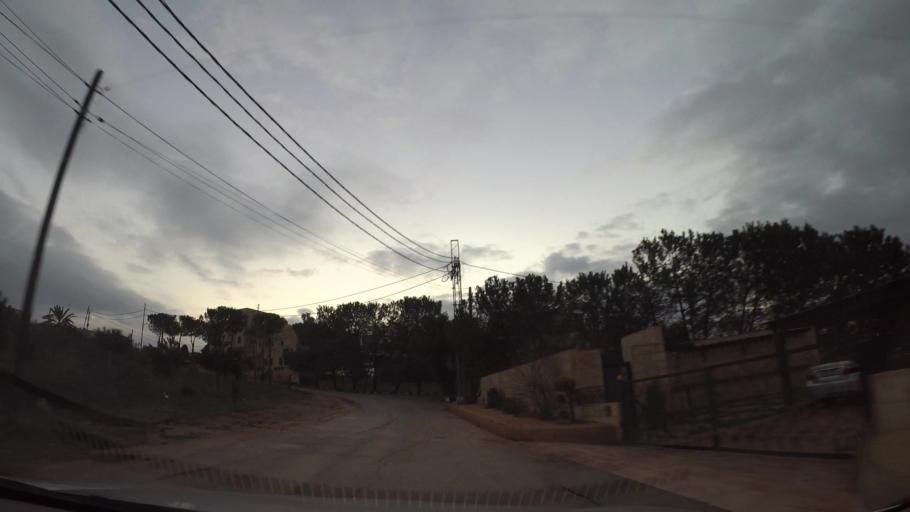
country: JO
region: Amman
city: Al Jubayhah
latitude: 32.0313
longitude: 35.8107
